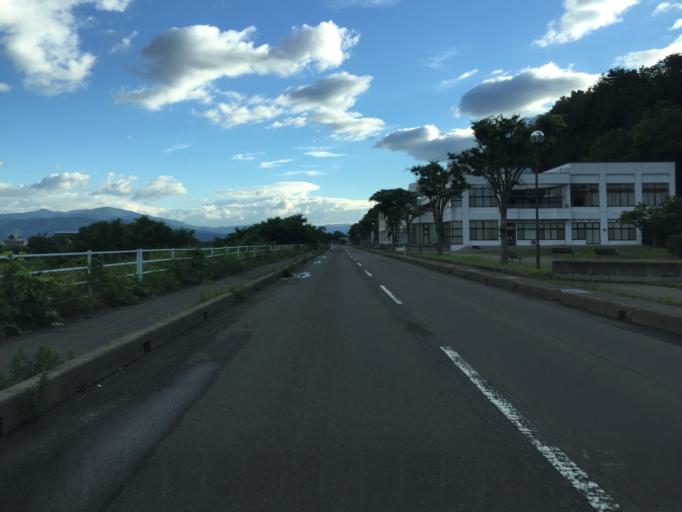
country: JP
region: Fukushima
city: Fukushima-shi
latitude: 37.7646
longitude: 140.4916
